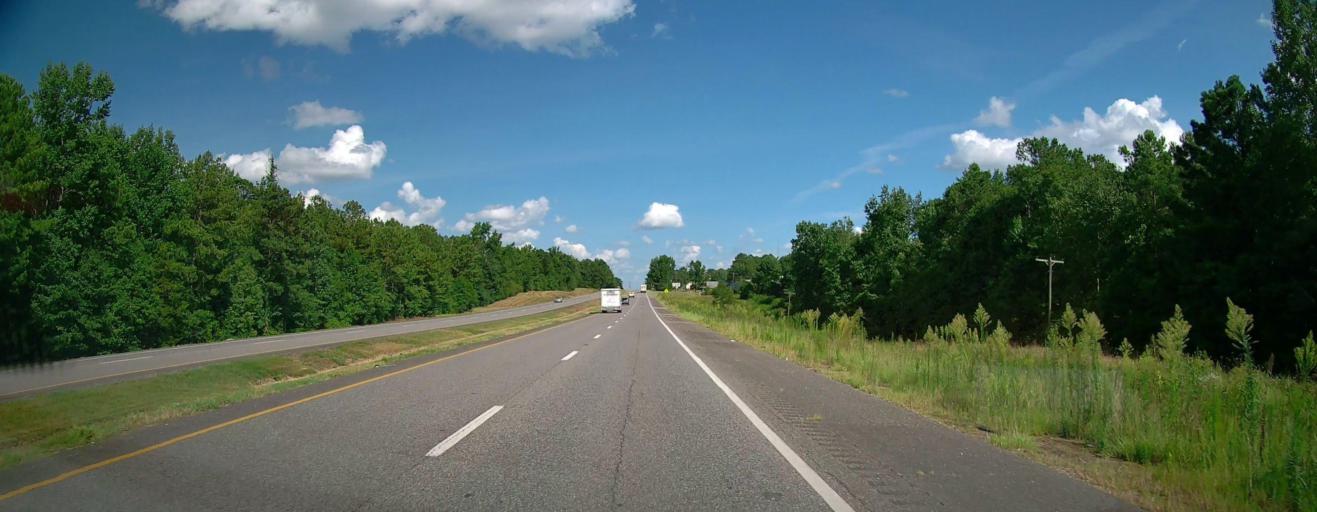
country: US
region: Alabama
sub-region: Tuscaloosa County
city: Northport
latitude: 33.2549
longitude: -87.6925
